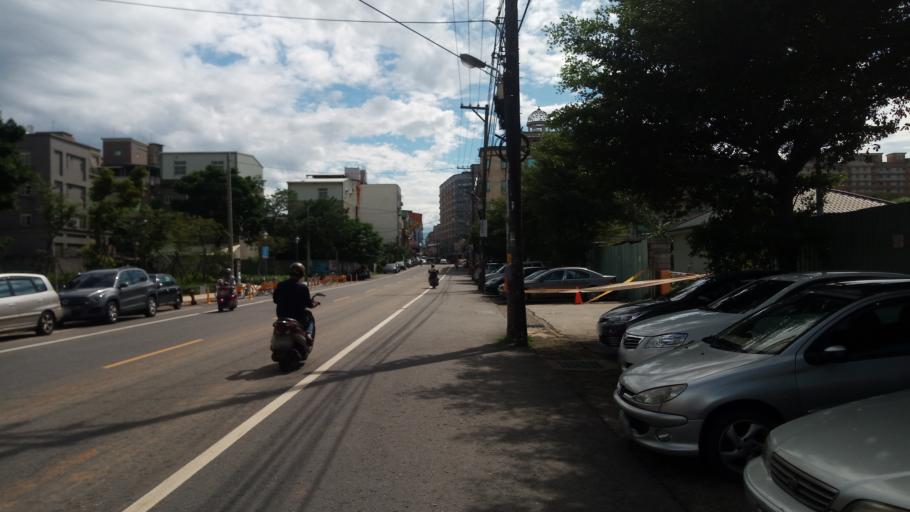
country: TW
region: Taiwan
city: Daxi
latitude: 24.9409
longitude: 121.2499
